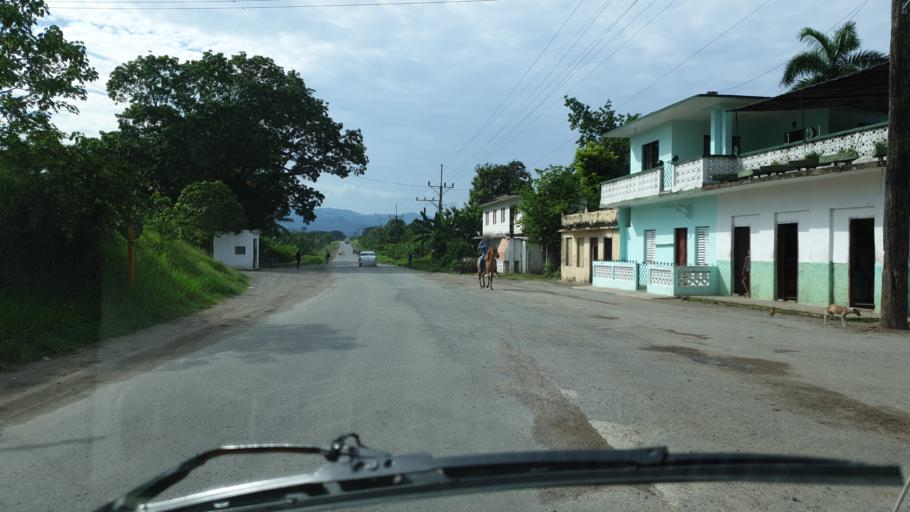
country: CU
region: Cienfuegos
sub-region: Municipio de Cienfuegos
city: Cumanayagua
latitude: 22.0753
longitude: -80.3115
